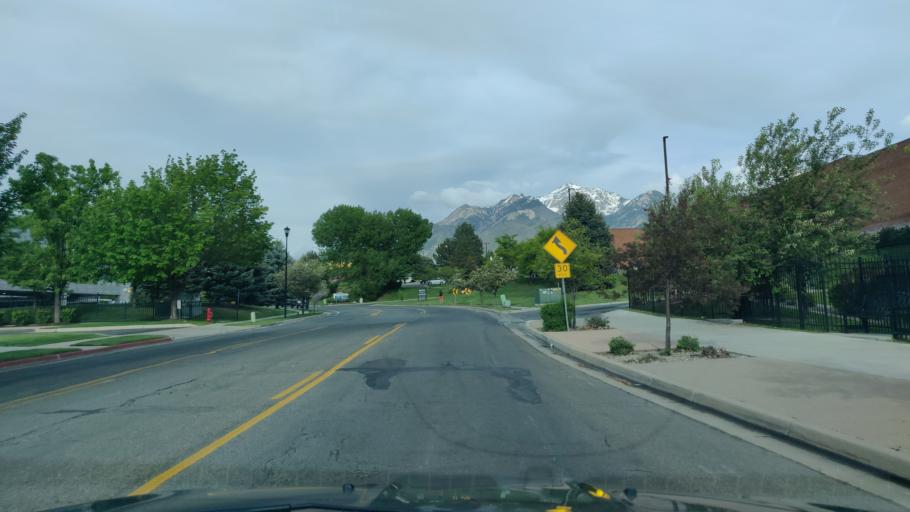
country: US
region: Utah
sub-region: Salt Lake County
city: Little Cottonwood Creek Valley
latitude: 40.6096
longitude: -111.8563
